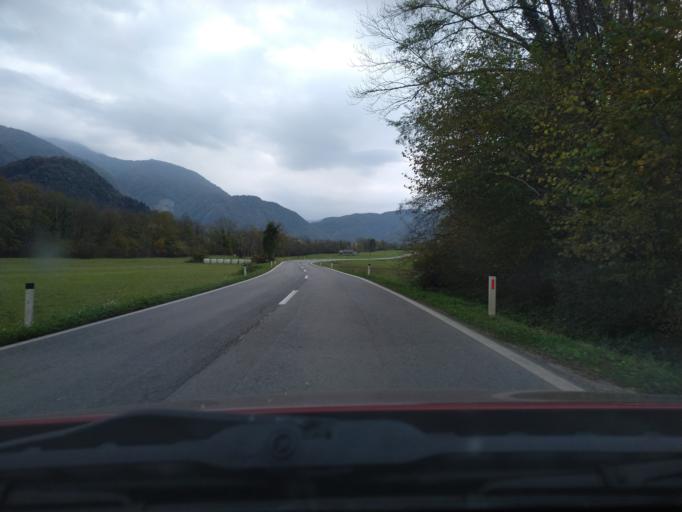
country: SI
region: Tolmin
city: Tolmin
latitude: 46.1896
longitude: 13.7018
